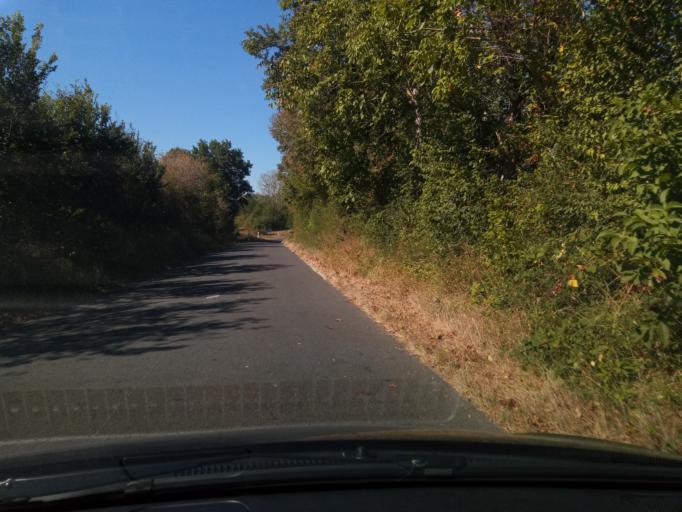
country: FR
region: Poitou-Charentes
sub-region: Departement de la Vienne
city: Montmorillon
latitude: 46.4782
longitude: 0.8967
